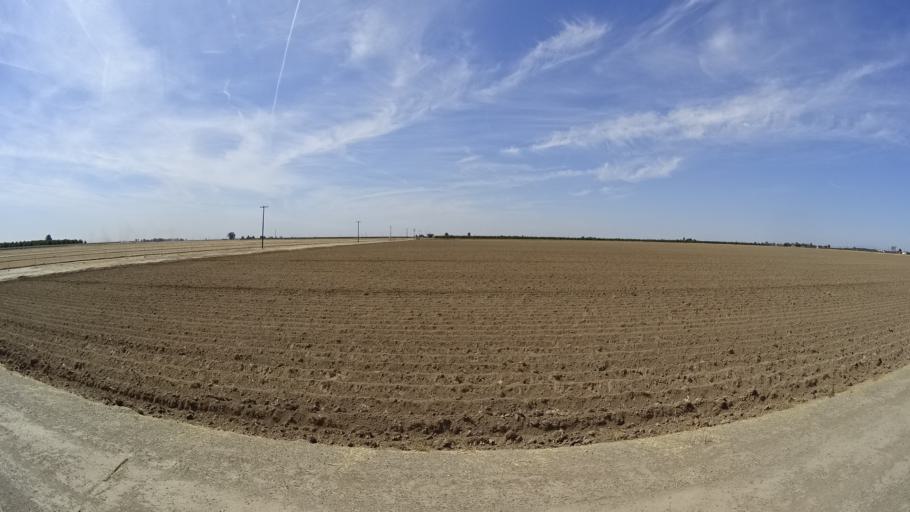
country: US
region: California
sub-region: Kings County
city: Hanford
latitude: 36.3574
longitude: -119.5567
